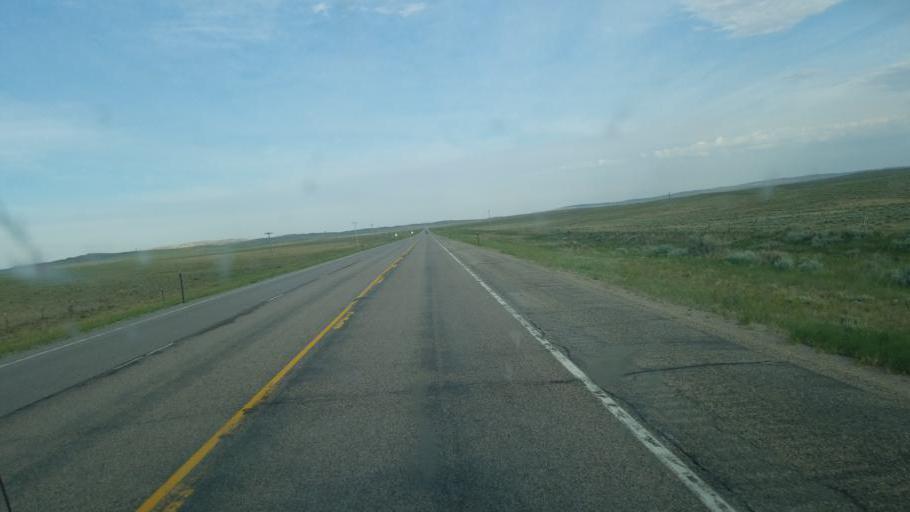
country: US
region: Wyoming
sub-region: Natrona County
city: Mills
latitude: 43.0318
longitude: -106.9047
